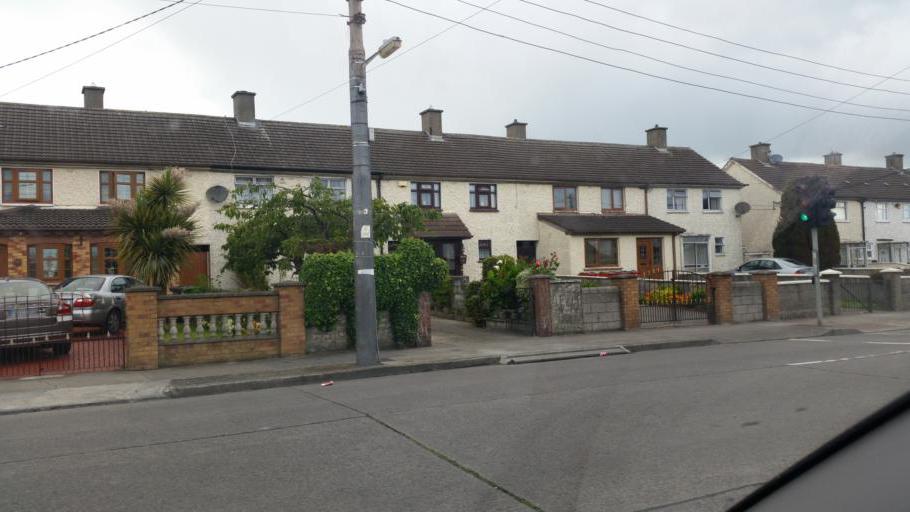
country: IE
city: Bonnybrook
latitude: 53.3992
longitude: -6.2057
